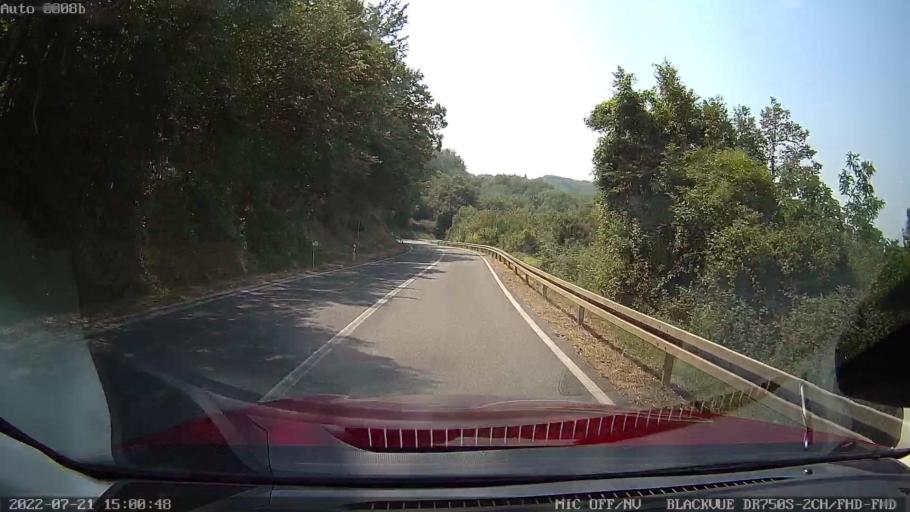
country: HR
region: Istarska
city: Pazin
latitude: 45.2268
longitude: 13.9550
